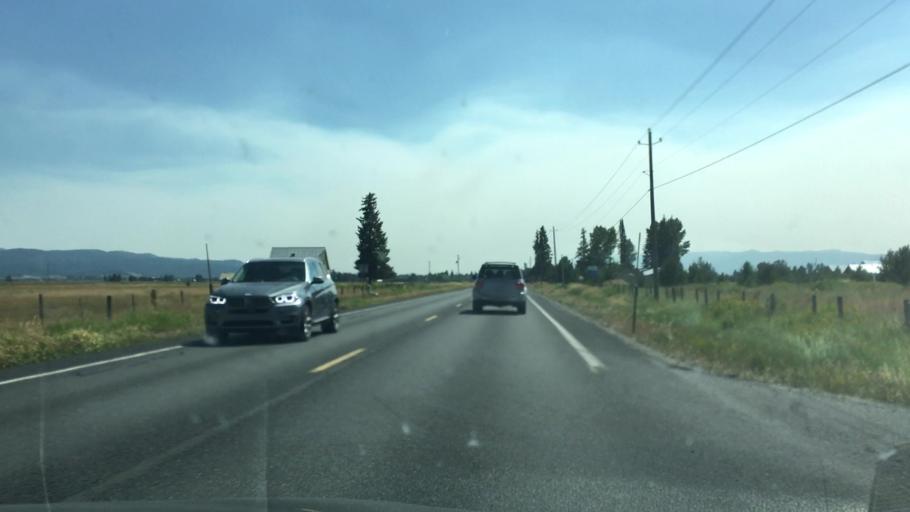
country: US
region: Idaho
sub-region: Valley County
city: McCall
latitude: 44.7489
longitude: -116.0784
